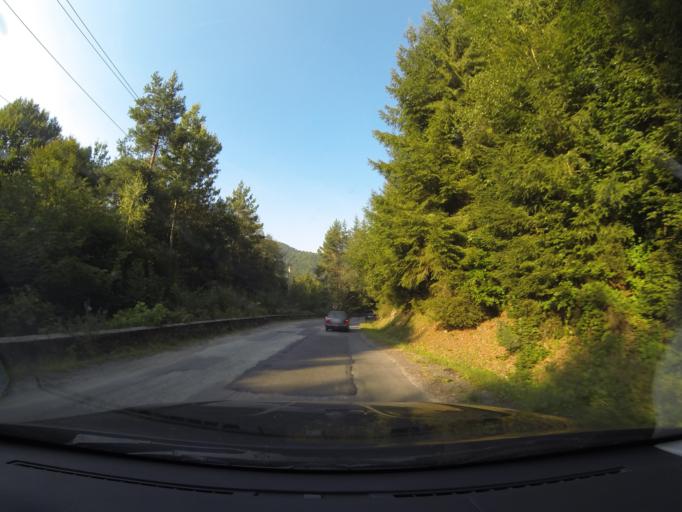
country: RO
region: Arges
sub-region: Comuna Arefu
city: Arefu
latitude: 45.3997
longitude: 24.6395
